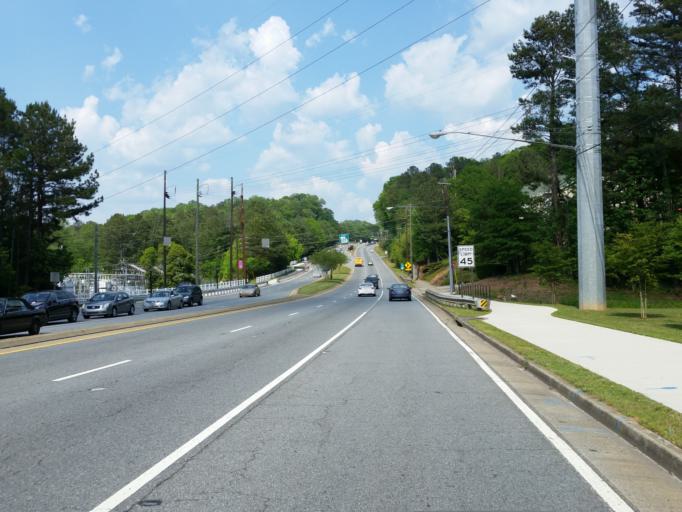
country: US
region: Georgia
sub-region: Fulton County
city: Roswell
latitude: 34.0118
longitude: -84.3739
